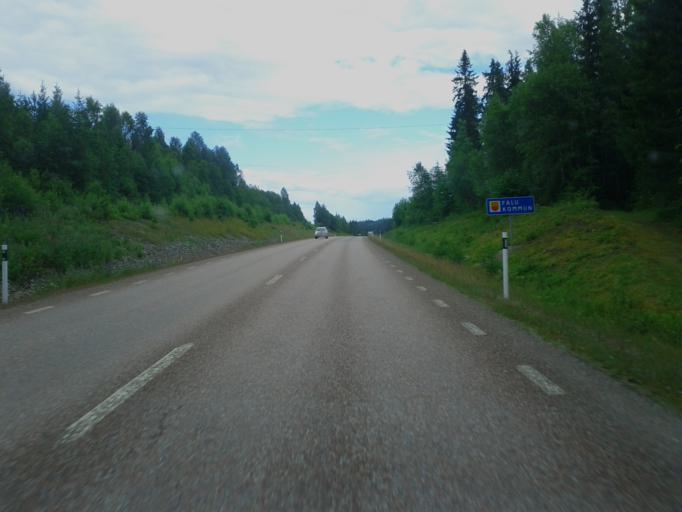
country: SE
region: Dalarna
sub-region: Faluns Kommun
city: Bjursas
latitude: 60.7572
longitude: 15.3373
